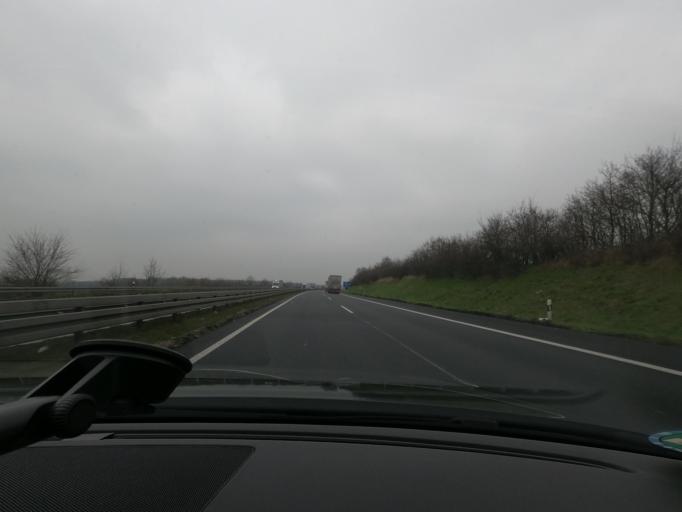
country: DE
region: North Rhine-Westphalia
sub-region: Regierungsbezirk Dusseldorf
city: Nettetal
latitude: 51.3046
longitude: 6.2366
